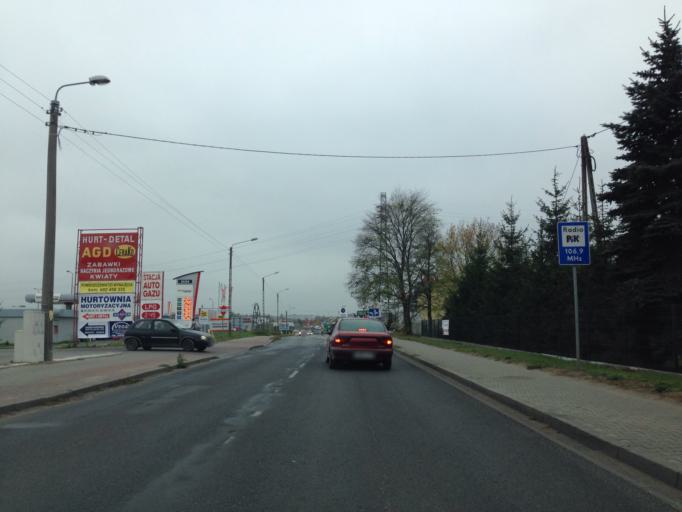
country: PL
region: Kujawsko-Pomorskie
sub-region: Powiat brodnicki
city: Brodnica
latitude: 53.2387
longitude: 19.3927
